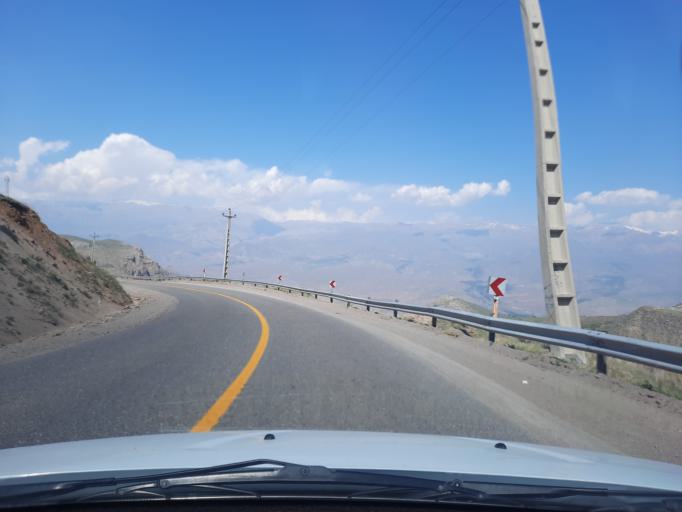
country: IR
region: Qazvin
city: Qazvin
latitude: 36.4036
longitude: 50.2224
